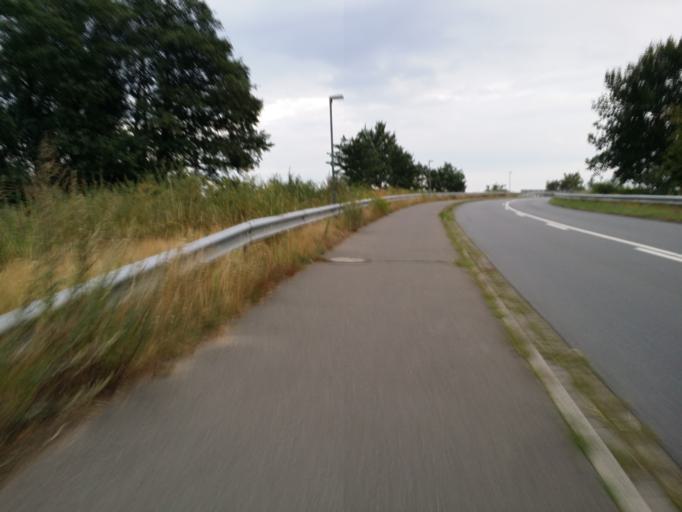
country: DE
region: Schleswig-Holstein
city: Heiligenstedten
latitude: 53.9379
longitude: 9.4705
